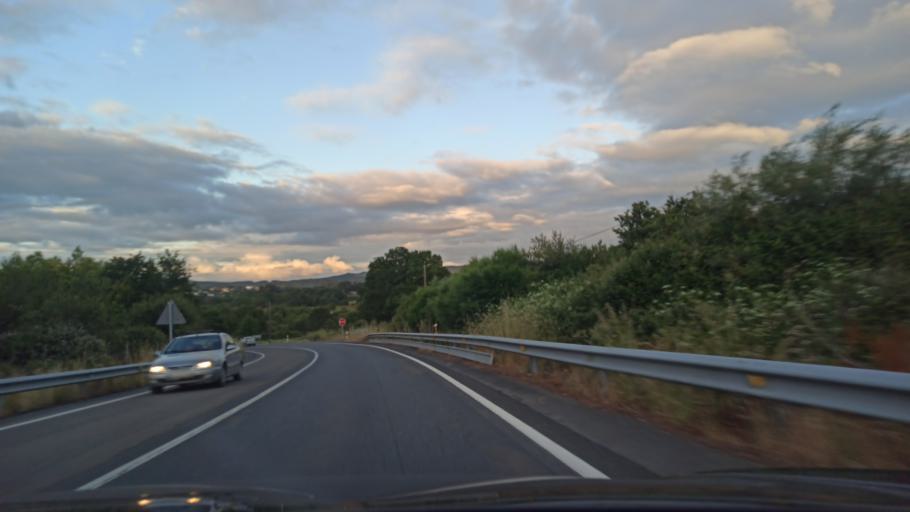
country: ES
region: Galicia
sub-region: Provincia de Lugo
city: Monterroso
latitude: 42.7887
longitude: -7.8620
